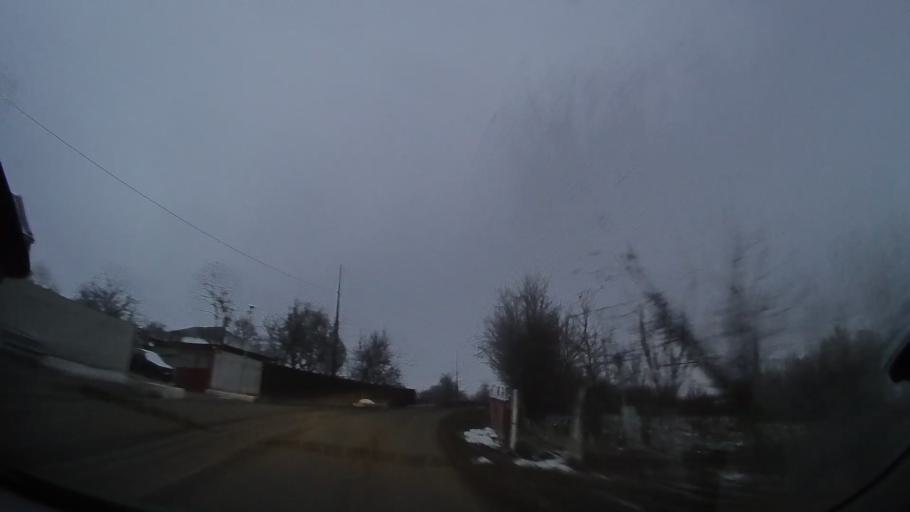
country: RO
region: Vaslui
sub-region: Comuna Vutcani
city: Vutcani
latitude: 46.4178
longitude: 27.9973
